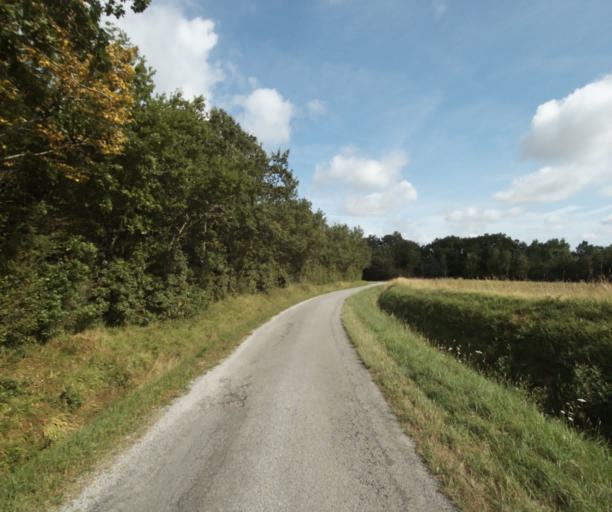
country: FR
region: Midi-Pyrenees
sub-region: Departement du Tarn
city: Soreze
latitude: 43.4690
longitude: 2.0842
